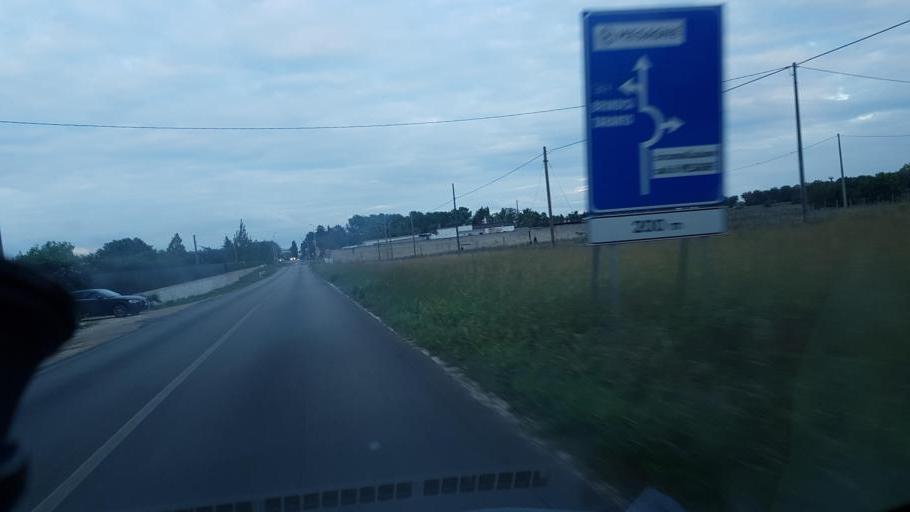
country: IT
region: Apulia
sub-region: Provincia di Brindisi
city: Mesagne
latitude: 40.5584
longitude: 17.7836
